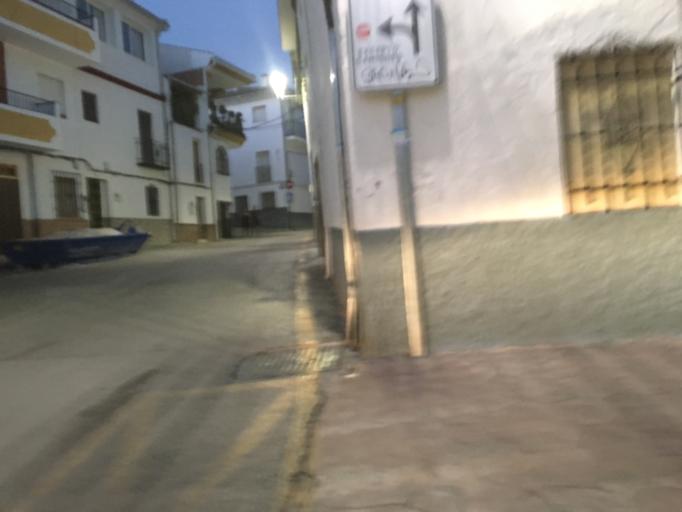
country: ES
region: Andalusia
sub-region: Provincia de Granada
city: Beas de Granada
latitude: 37.2177
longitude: -3.4817
